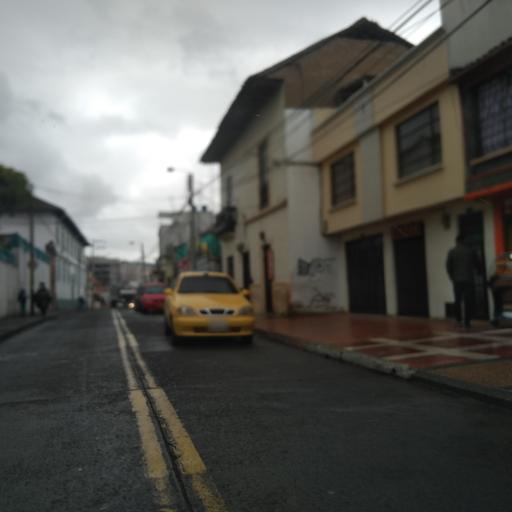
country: CO
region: Narino
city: Pasto
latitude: 1.2142
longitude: -77.2849
